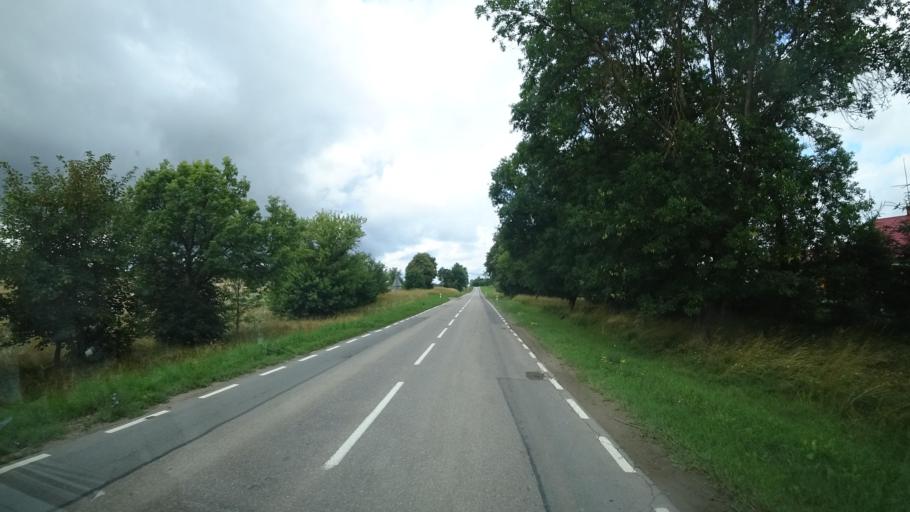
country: PL
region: Warmian-Masurian Voivodeship
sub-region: Powiat olecki
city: Kowale Oleckie
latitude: 54.0923
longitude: 22.4479
